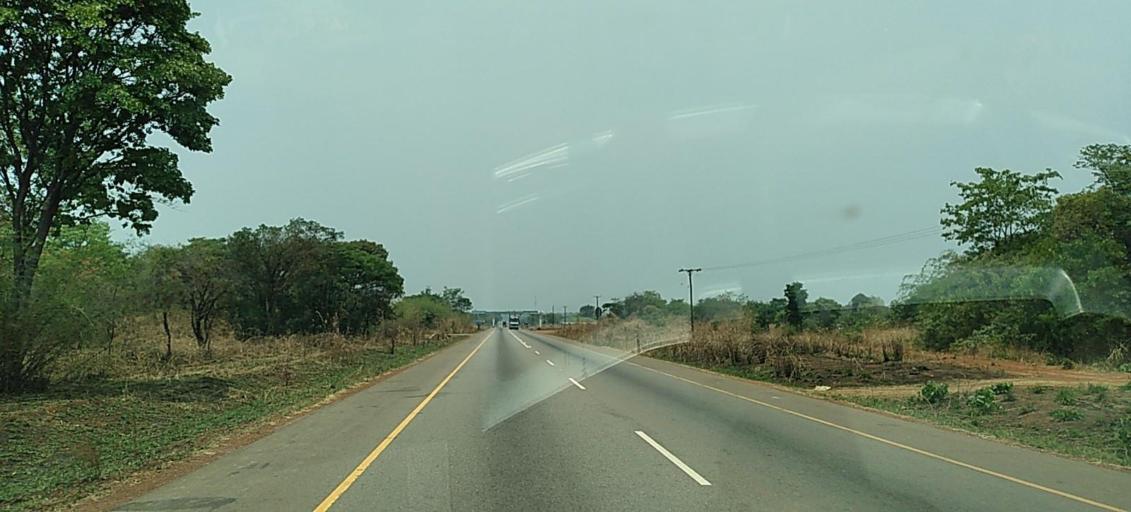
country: ZM
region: Copperbelt
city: Chingola
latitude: -12.5519
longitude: 27.6998
